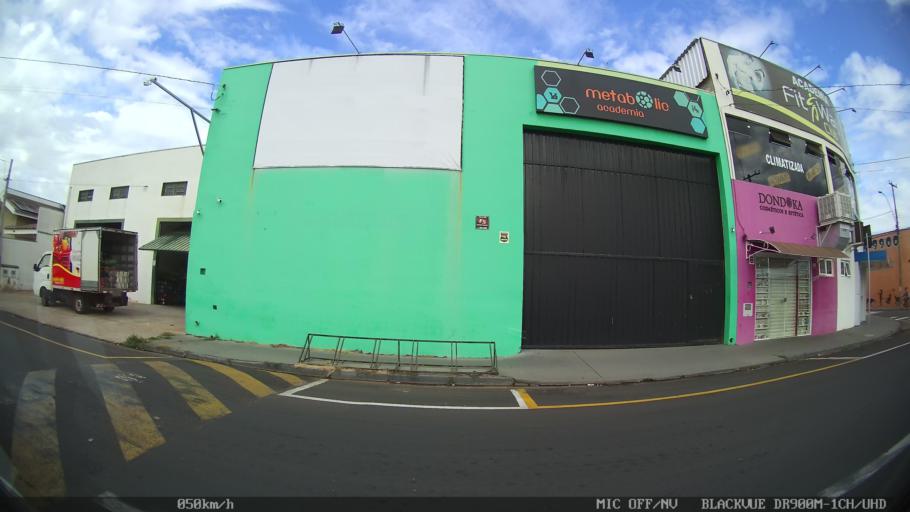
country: BR
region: Sao Paulo
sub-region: Sao Jose Do Rio Preto
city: Sao Jose do Rio Preto
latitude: -20.8043
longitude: -49.4963
